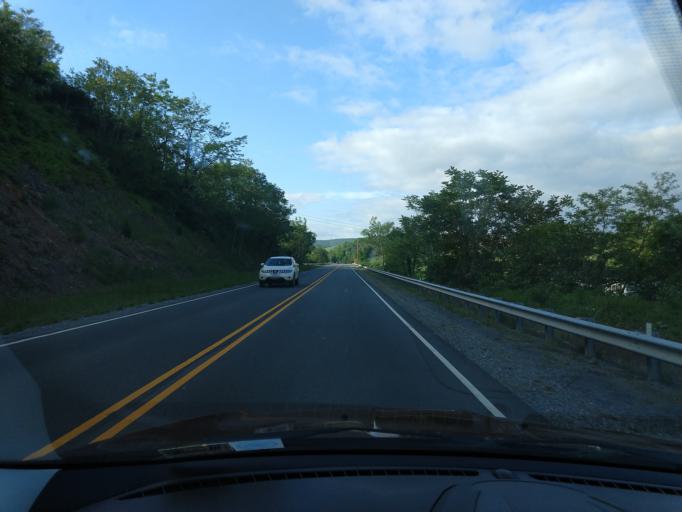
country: US
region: Virginia
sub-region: Wythe County
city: Wytheville
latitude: 36.8578
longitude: -80.9791
